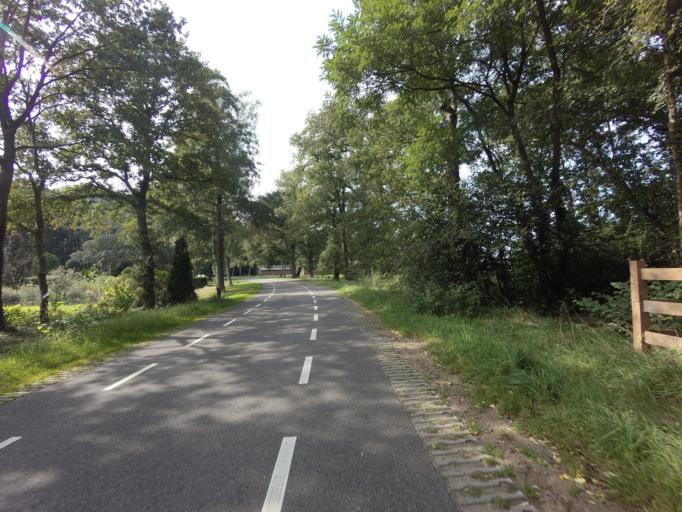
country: NL
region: Overijssel
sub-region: Gemeente Hof van Twente
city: Goor
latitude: 52.2620
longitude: 6.5842
